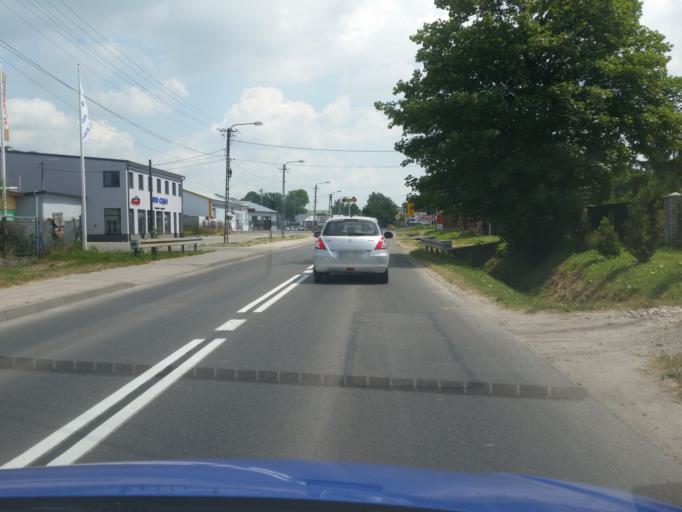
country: PL
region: Lesser Poland Voivodeship
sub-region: Powiat miechowski
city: Miechow
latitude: 50.3564
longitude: 20.0406
